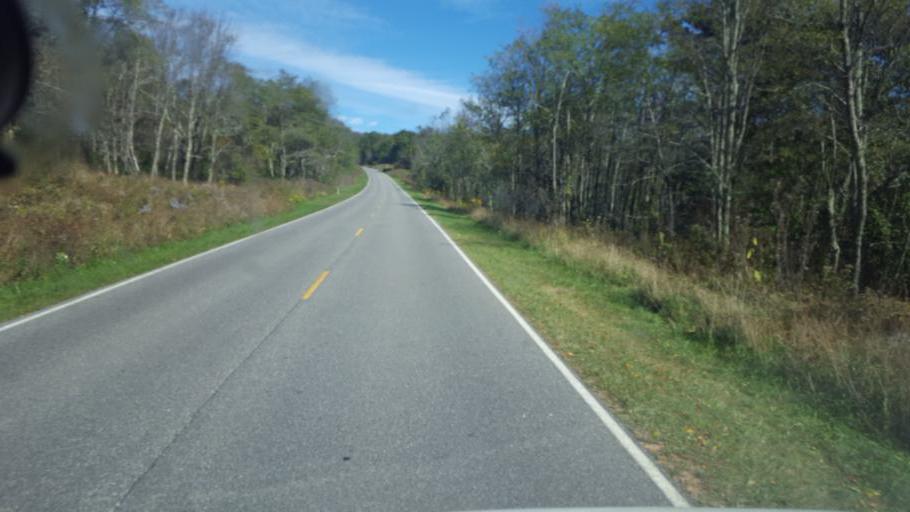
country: US
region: Virginia
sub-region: Page County
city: Stanley
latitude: 38.5027
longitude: -78.4435
